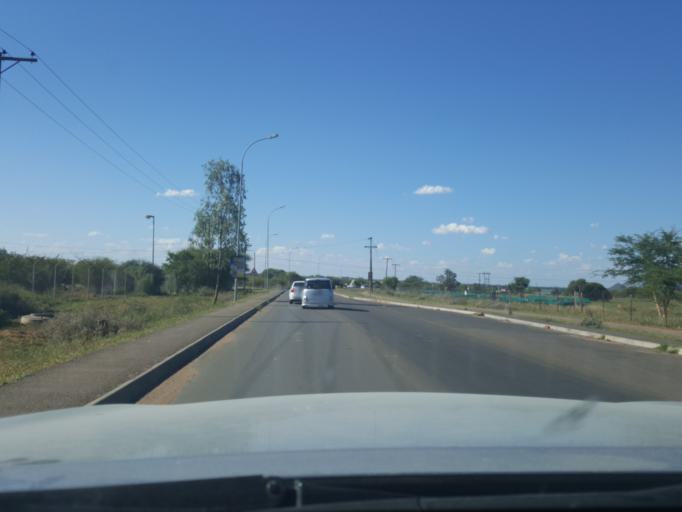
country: BW
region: South East
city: Gaborone
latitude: -24.6101
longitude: 25.9526
